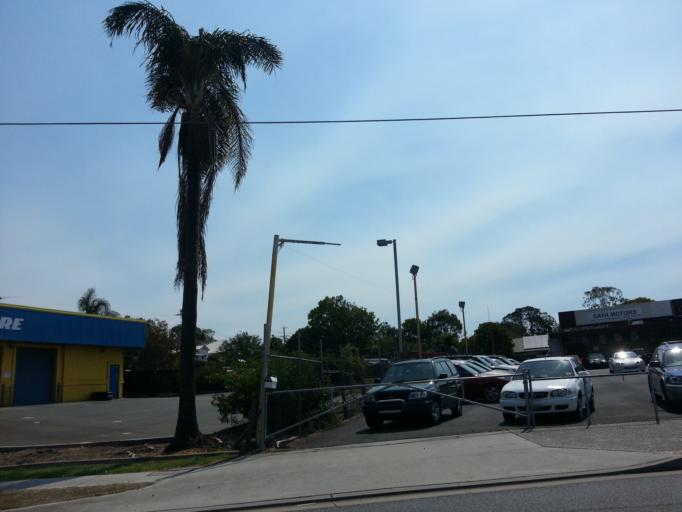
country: AU
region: Queensland
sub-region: Brisbane
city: Gordon Park
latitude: -27.4037
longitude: 153.0317
